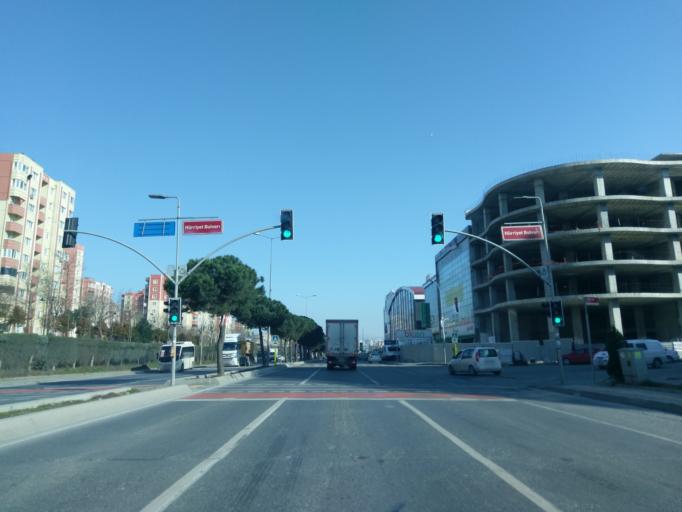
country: TR
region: Istanbul
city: Basaksehir
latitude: 41.1022
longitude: 28.7934
